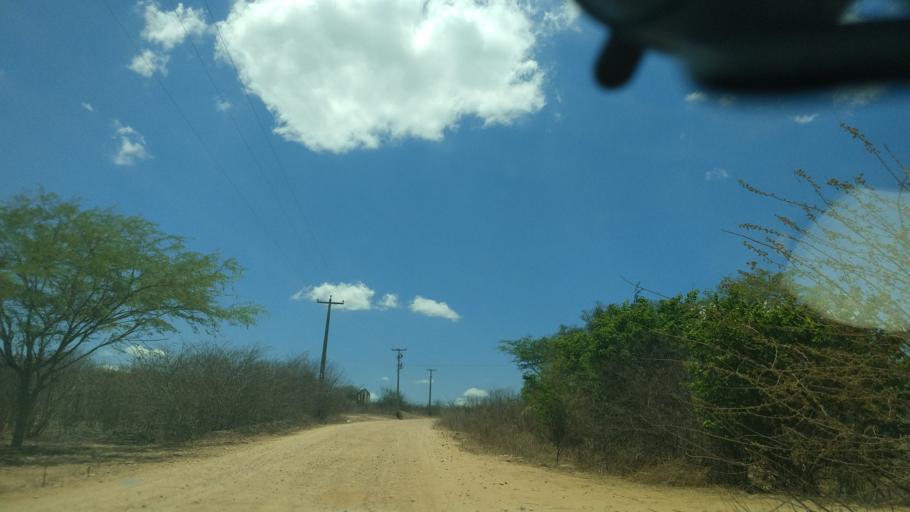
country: BR
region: Rio Grande do Norte
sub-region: Cerro Cora
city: Cerro Cora
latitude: -6.0210
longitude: -36.3317
